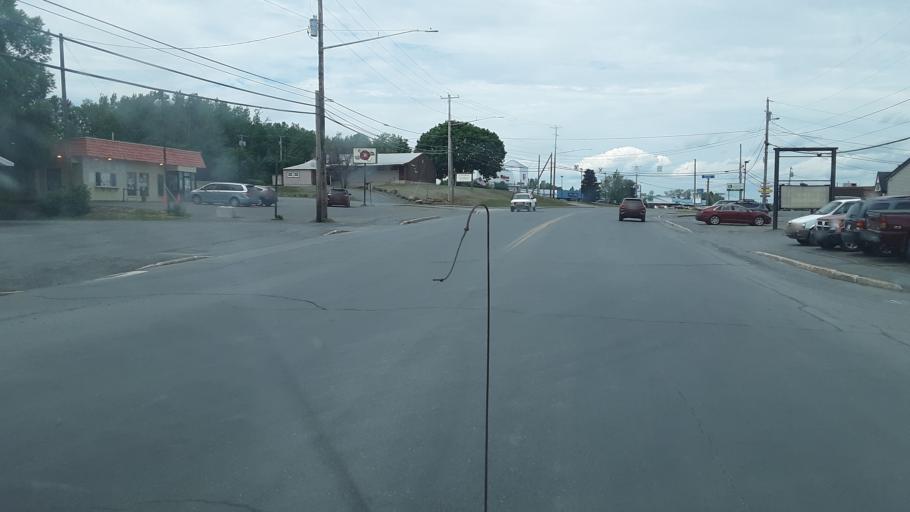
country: US
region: Maine
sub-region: Aroostook County
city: Caribou
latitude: 46.8668
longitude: -68.0049
